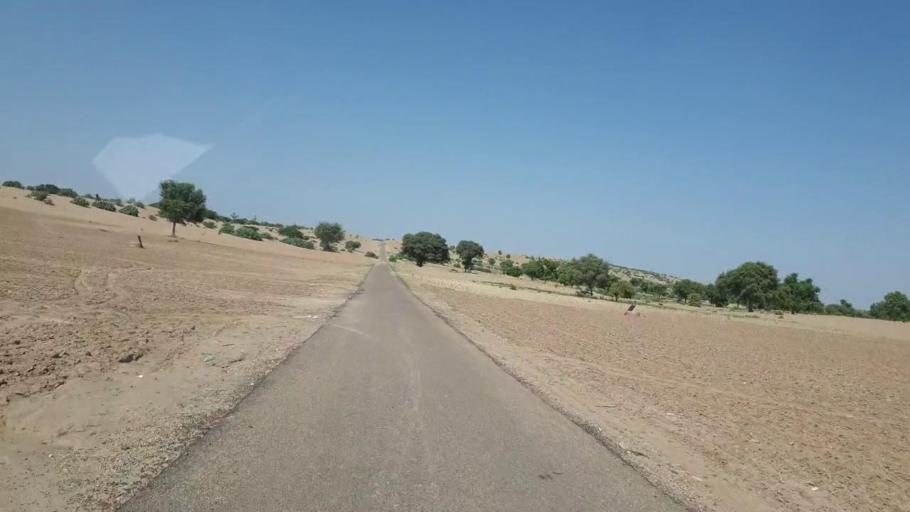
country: PK
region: Sindh
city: Chor
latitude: 25.6097
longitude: 70.3162
